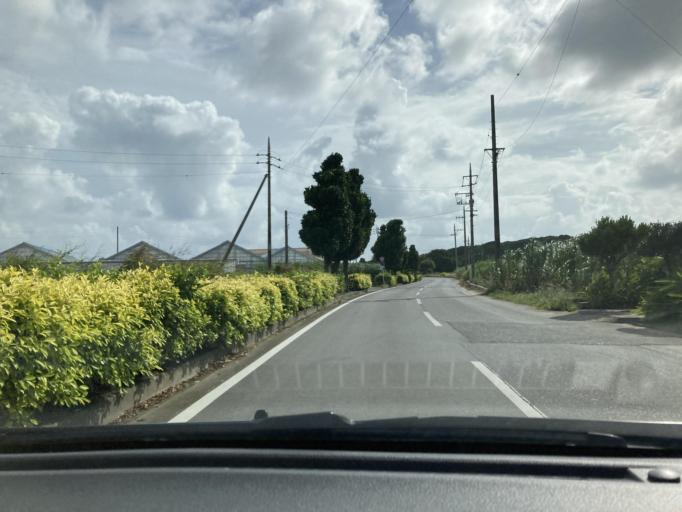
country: JP
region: Okinawa
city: Itoman
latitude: 26.0885
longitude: 127.6938
